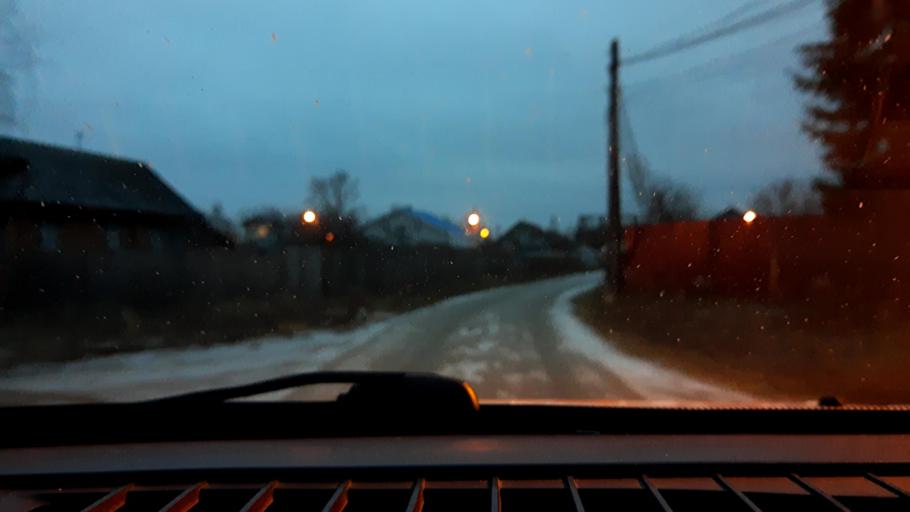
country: RU
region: Nizjnij Novgorod
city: Gorbatovka
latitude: 56.3881
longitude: 43.7518
